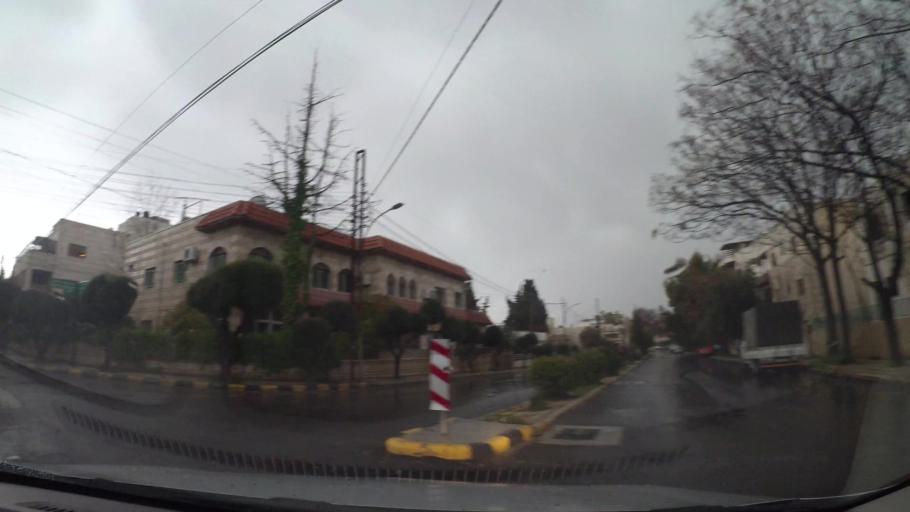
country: JO
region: Amman
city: Umm as Summaq
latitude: 31.8976
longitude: 35.8551
